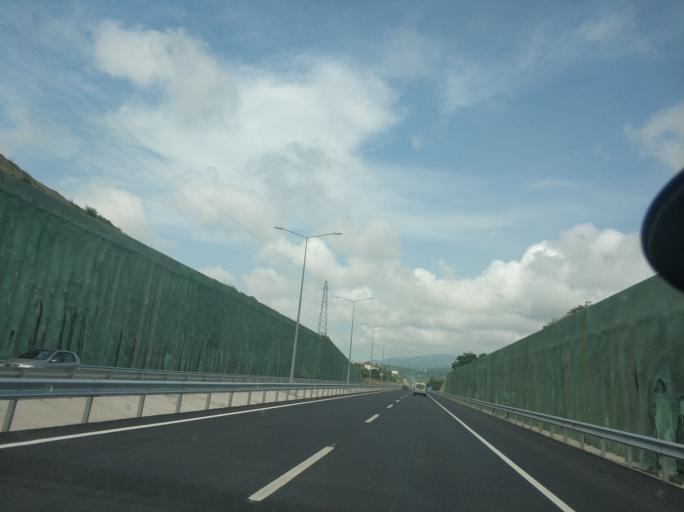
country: TR
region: Ordu
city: Ordu
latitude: 40.9550
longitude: 37.8709
